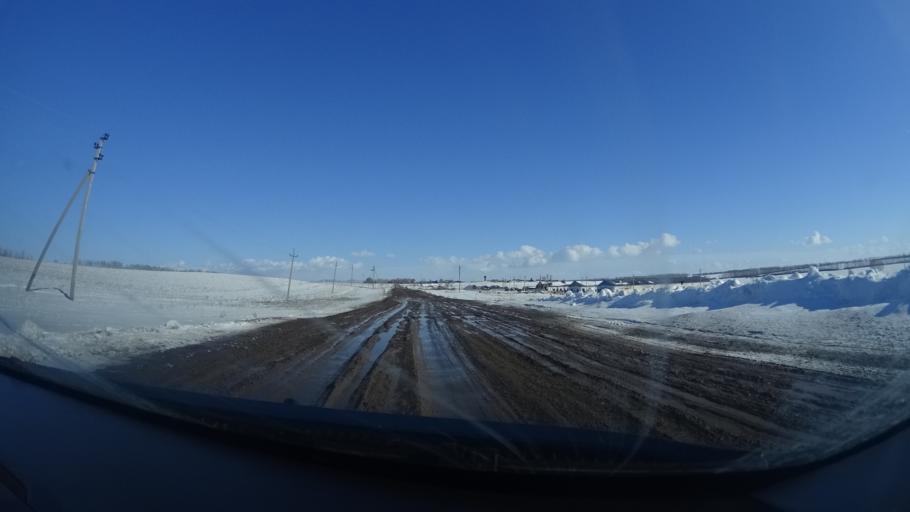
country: RU
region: Bashkortostan
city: Chishmy
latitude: 54.5991
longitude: 55.2393
